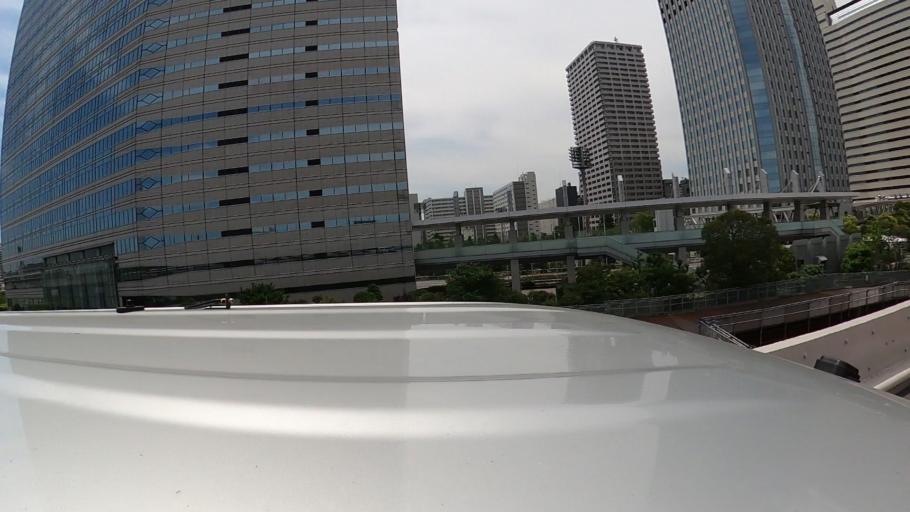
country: JP
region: Tokyo
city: Tokyo
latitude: 35.6205
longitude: 139.7516
